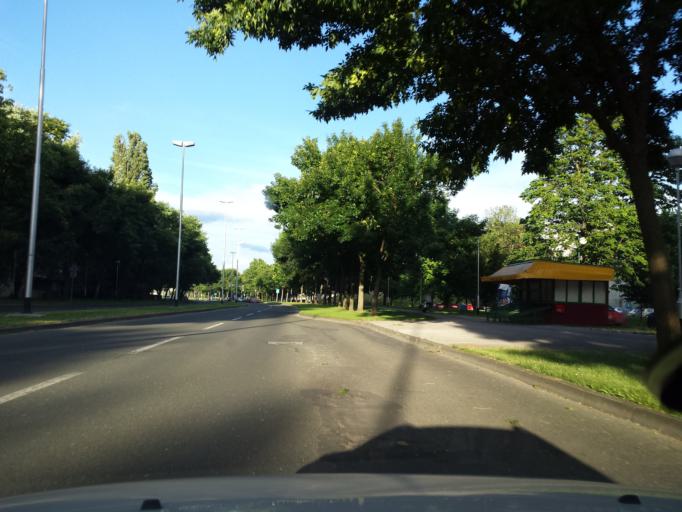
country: HR
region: Grad Zagreb
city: Novi Zagreb
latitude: 45.7729
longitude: 15.9990
